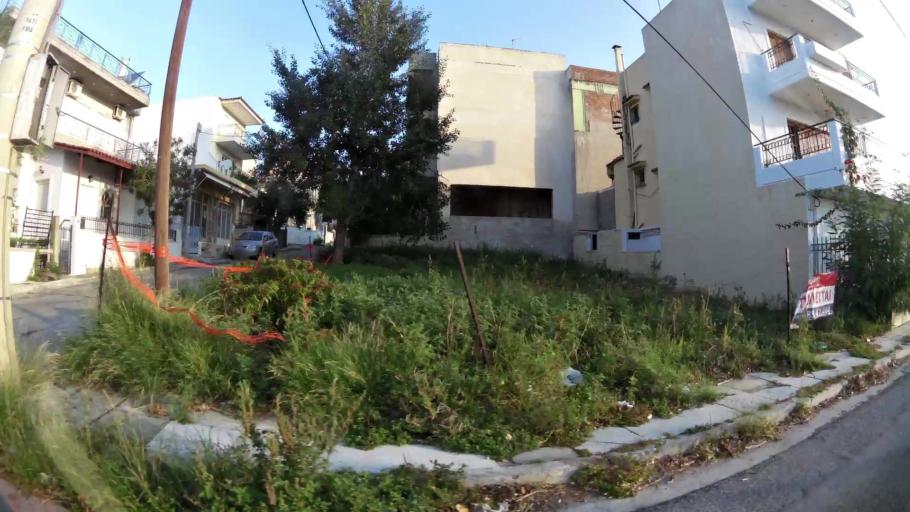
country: GR
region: Attica
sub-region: Nomarchia Athinas
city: Kamateron
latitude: 38.0533
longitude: 23.7168
